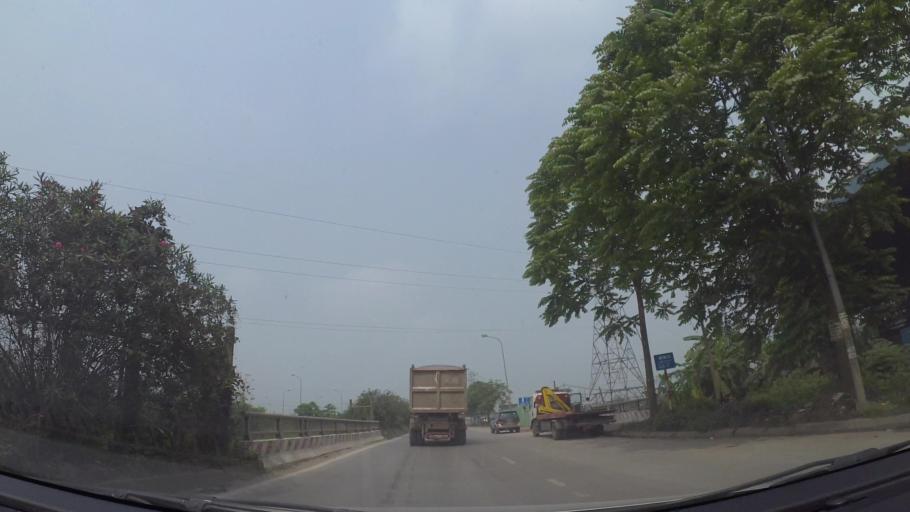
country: VN
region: Ha Noi
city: Quoc Oai
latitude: 21.0028
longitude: 105.6278
